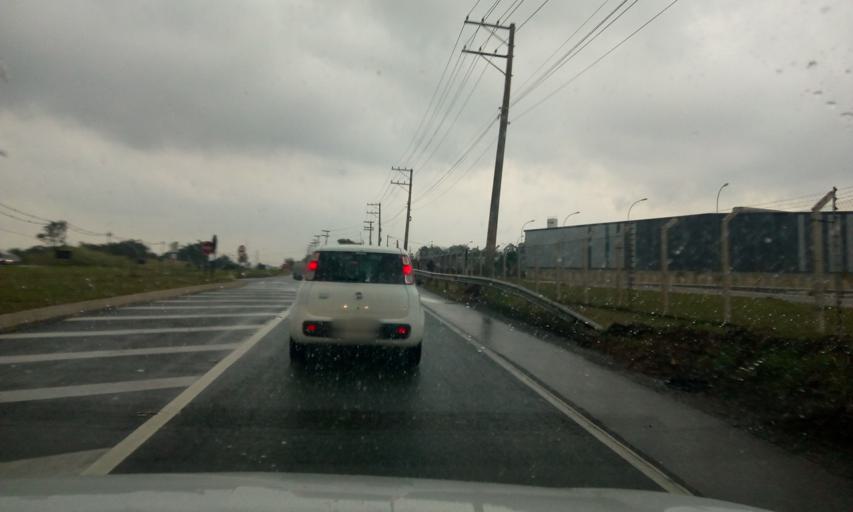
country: BR
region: Sao Paulo
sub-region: Itupeva
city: Itupeva
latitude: -23.1732
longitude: -46.9912
